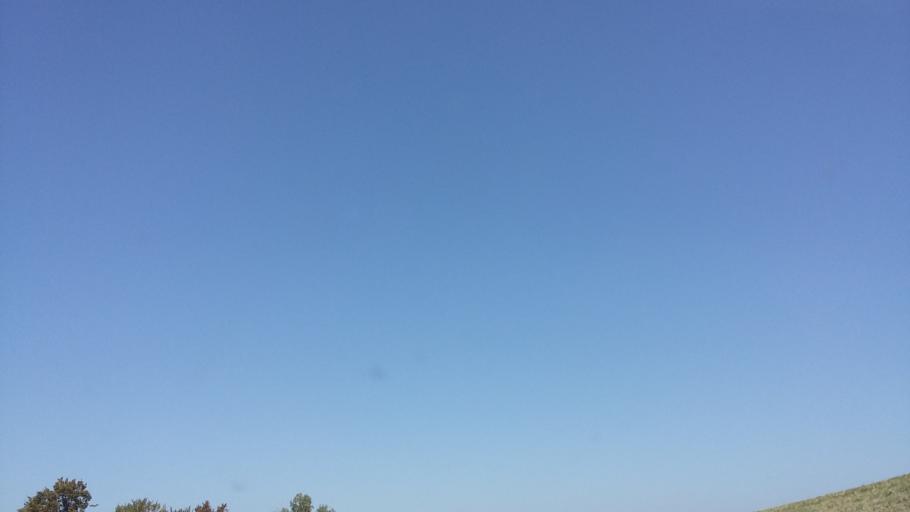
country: DE
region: Bavaria
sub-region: Swabia
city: Kleinaitingen
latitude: 48.2041
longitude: 10.8560
